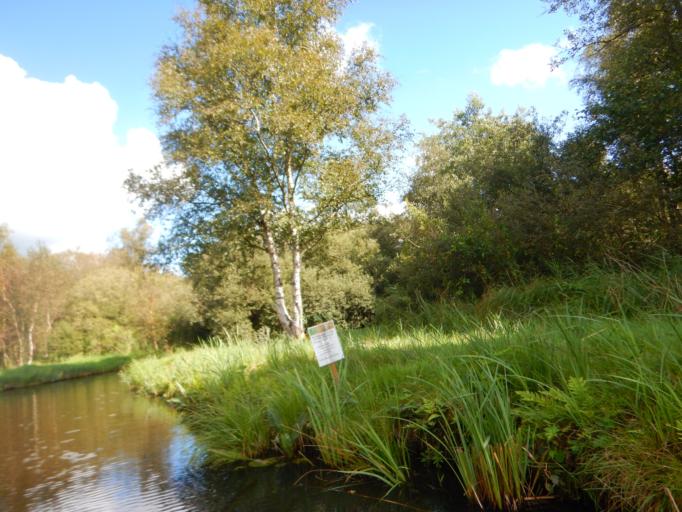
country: NL
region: Overijssel
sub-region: Gemeente Steenwijkerland
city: Oldemarkt
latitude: 52.7906
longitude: 5.9280
